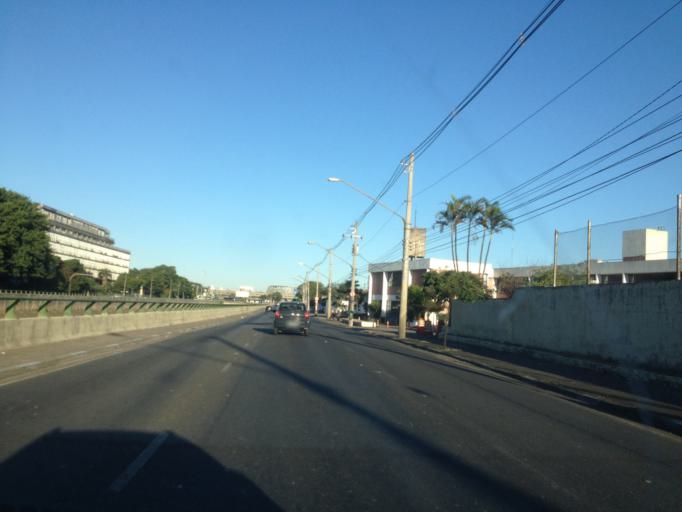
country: BR
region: Sao Paulo
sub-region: Sao Paulo
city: Sao Paulo
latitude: -23.5222
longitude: -46.6349
